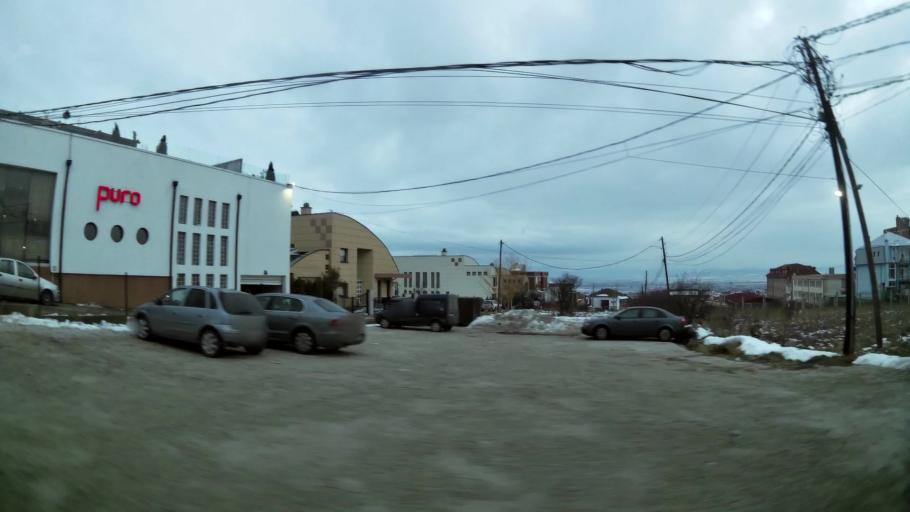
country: XK
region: Pristina
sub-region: Komuna e Prishtines
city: Pristina
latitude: 42.6303
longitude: 21.1618
